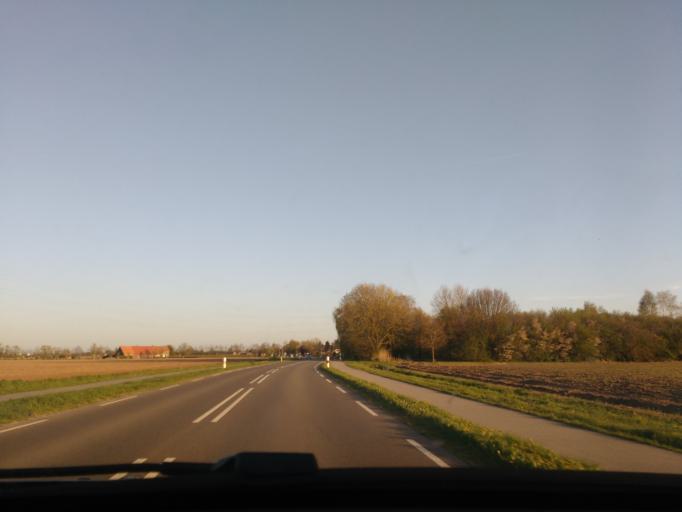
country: NL
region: Gelderland
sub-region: Gemeente Overbetuwe
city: Elst
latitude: 51.9368
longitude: 5.8351
